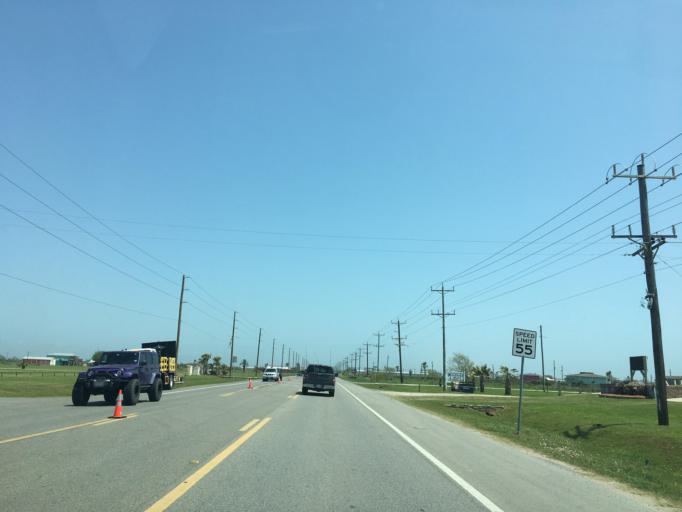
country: US
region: Texas
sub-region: Galveston County
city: Bolivar Peninsula
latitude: 29.4439
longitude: -94.6634
